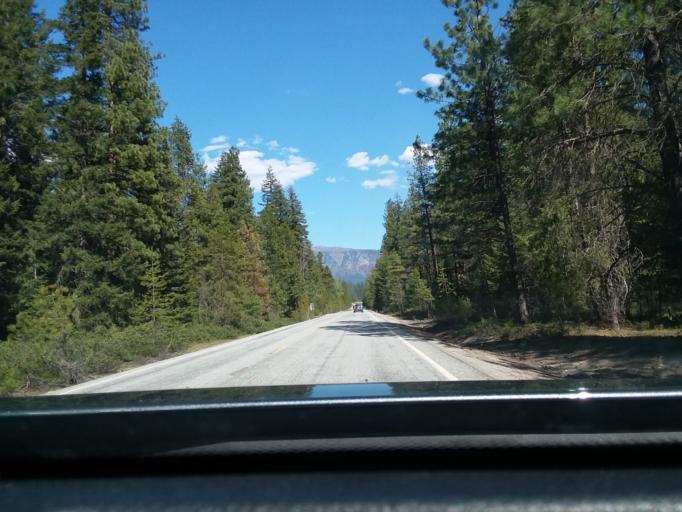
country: US
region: Washington
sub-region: Chelan County
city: Leavenworth
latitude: 47.8036
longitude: -120.7074
